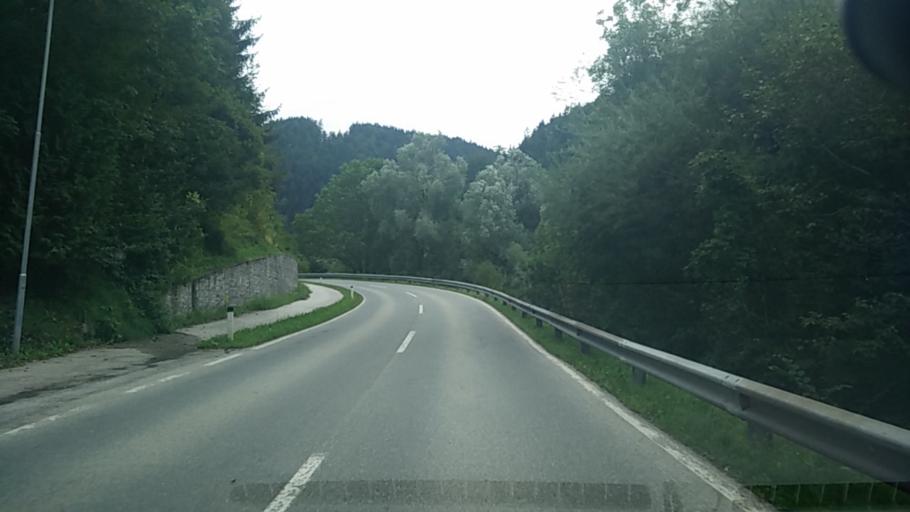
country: AT
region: Carinthia
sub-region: Politischer Bezirk Volkermarkt
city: Bad Eisenkappel
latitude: 46.4930
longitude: 14.5842
